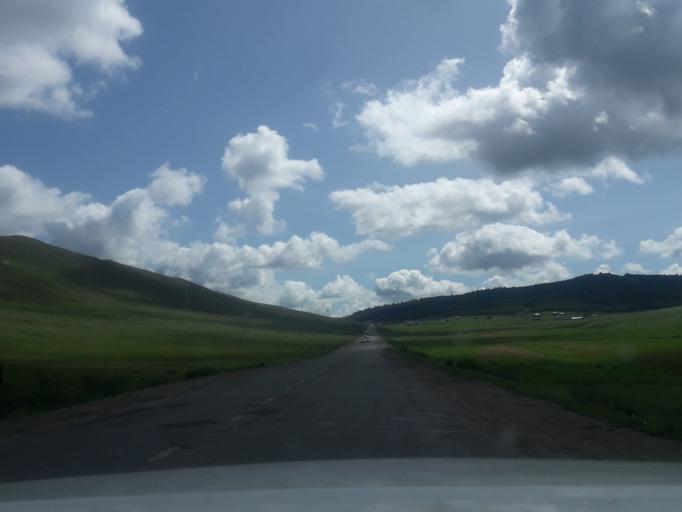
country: MN
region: Central Aimak
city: Ihsueuej
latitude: 48.1578
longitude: 106.4057
